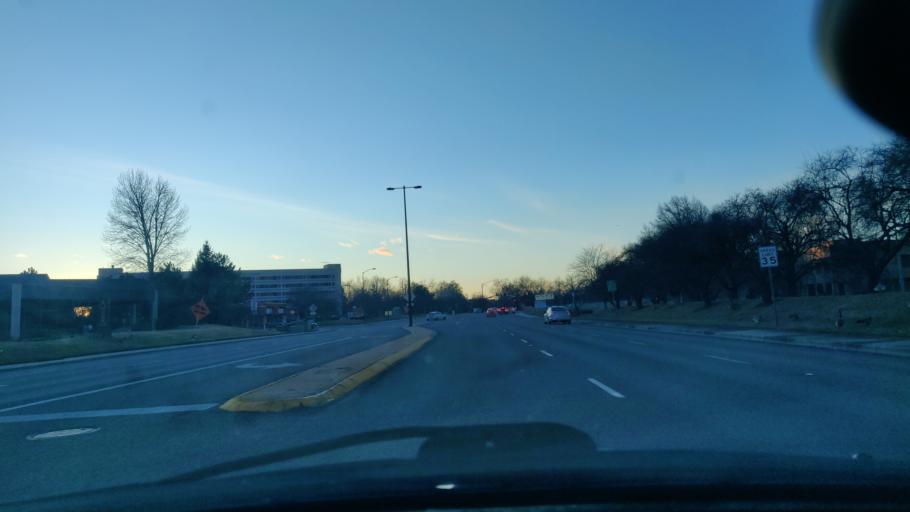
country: US
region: Idaho
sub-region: Ada County
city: Boise
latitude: 43.5987
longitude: -116.1839
